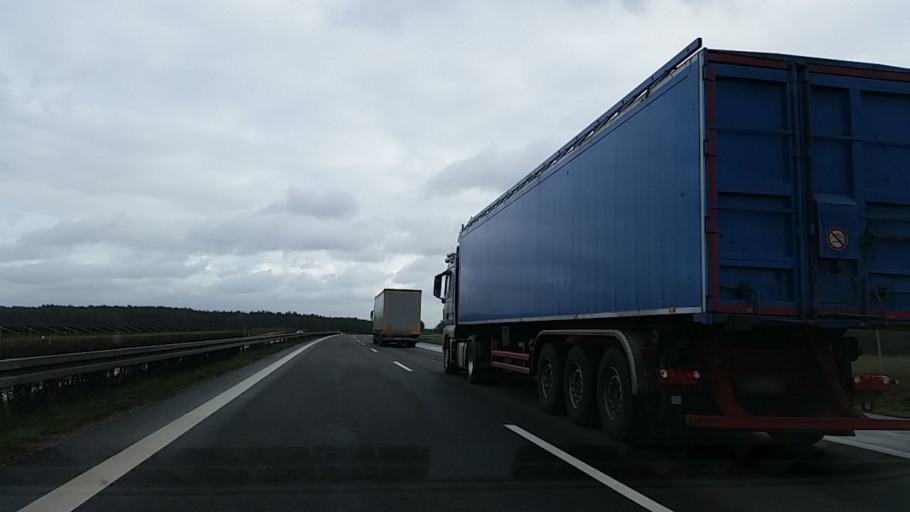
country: DE
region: Brandenburg
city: Heiligengrabe
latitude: 53.1675
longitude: 12.3682
